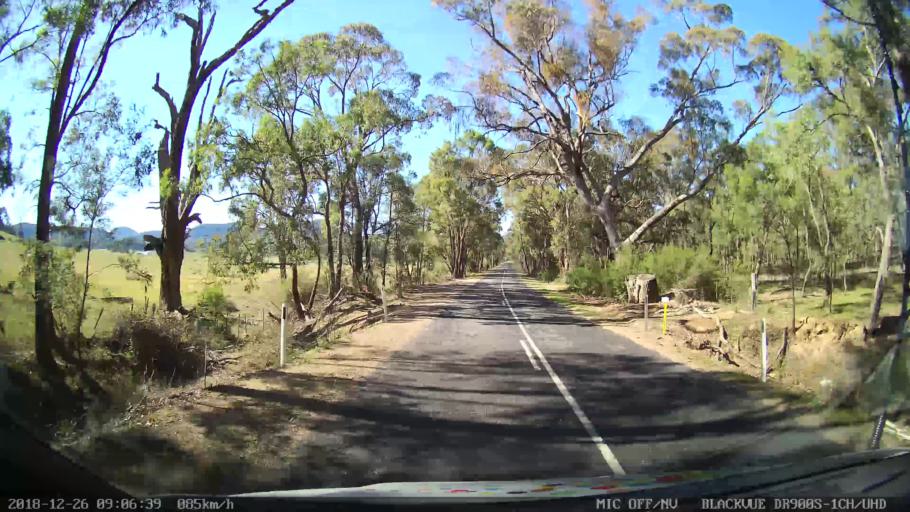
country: AU
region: New South Wales
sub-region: Mid-Western Regional
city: Kandos
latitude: -32.6968
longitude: 150.0059
